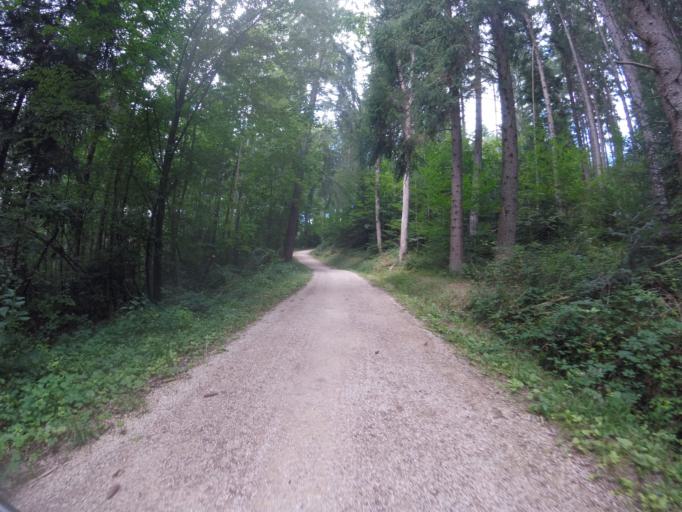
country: DE
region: Baden-Wuerttemberg
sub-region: Regierungsbezirk Stuttgart
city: Mutlangen
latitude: 48.8156
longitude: 9.7936
